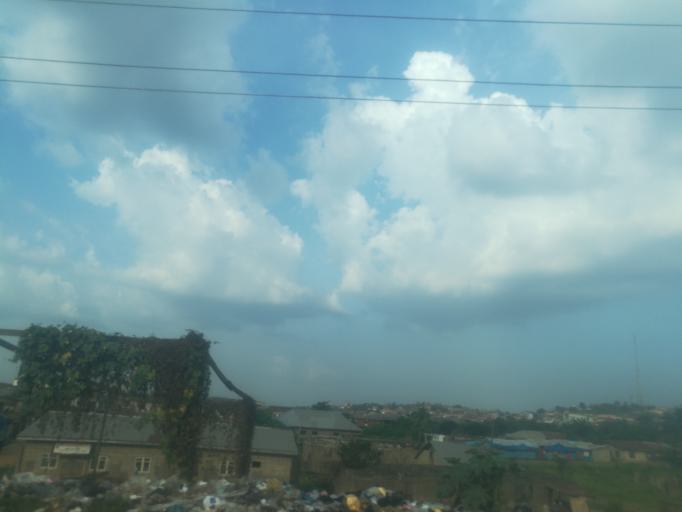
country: NG
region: Ogun
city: Abeokuta
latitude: 7.1498
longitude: 3.3240
